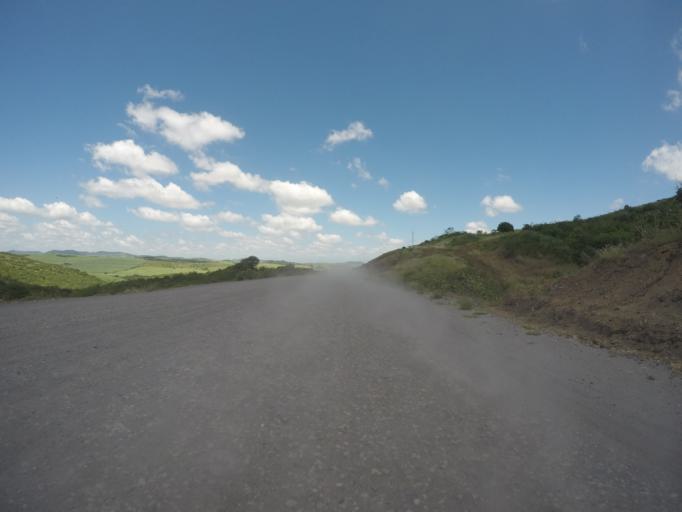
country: ZA
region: KwaZulu-Natal
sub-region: uThungulu District Municipality
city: Empangeni
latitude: -28.6296
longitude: 31.7596
